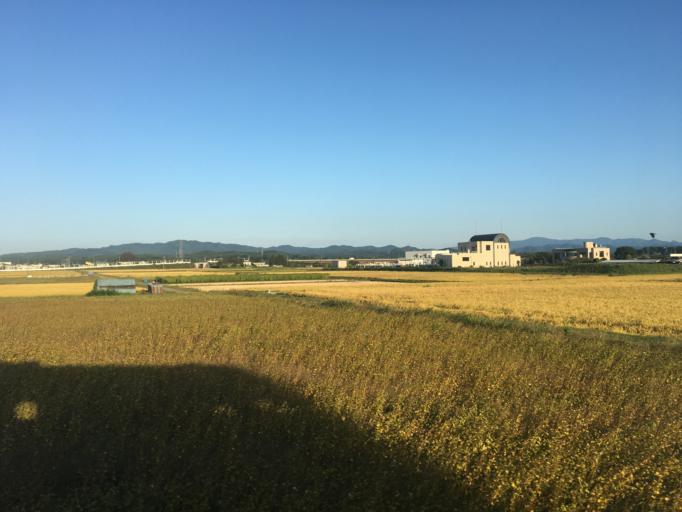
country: JP
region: Akita
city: Takanosu
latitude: 40.2180
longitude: 140.3553
